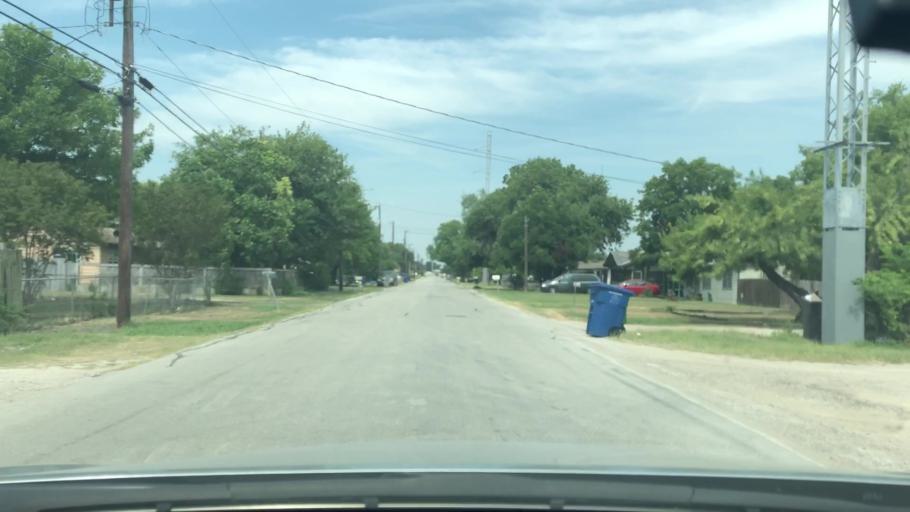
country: US
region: Texas
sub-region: Bexar County
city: Windcrest
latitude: 29.4921
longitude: -98.3948
